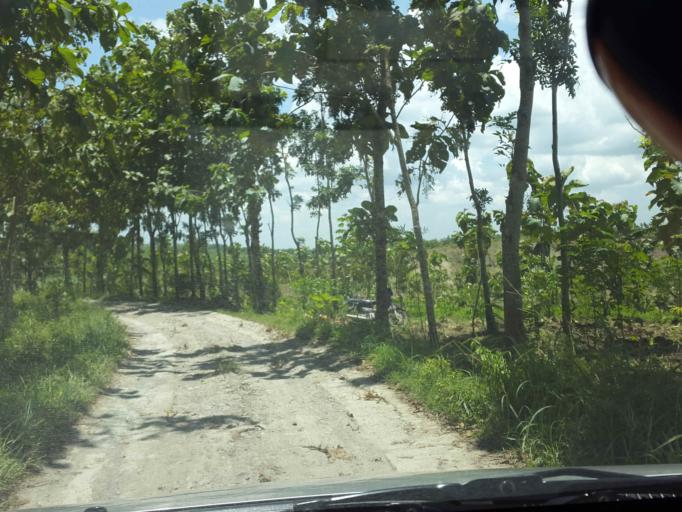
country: ID
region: Central Java
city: Sragen
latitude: -7.2718
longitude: 111.1307
